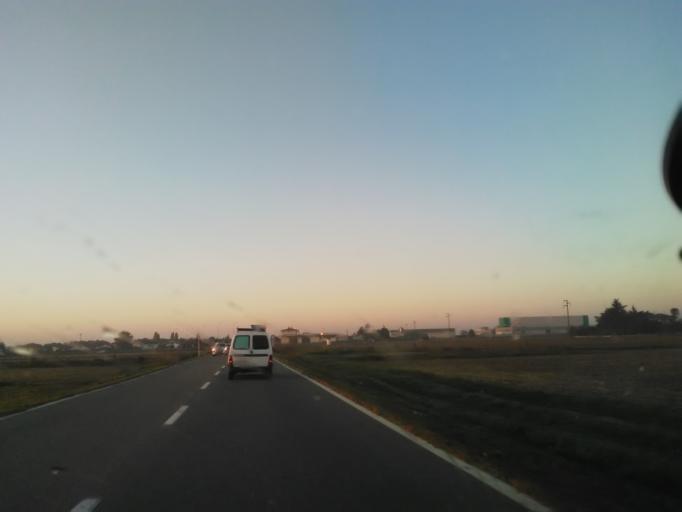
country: IT
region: Piedmont
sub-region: Provincia di Vercelli
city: Tronzano Vercellese
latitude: 45.3502
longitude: 8.1685
